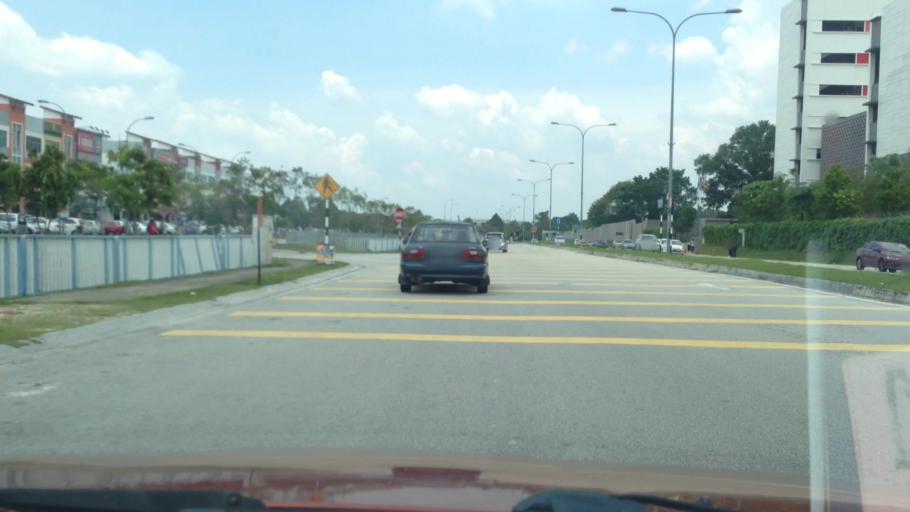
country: MY
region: Selangor
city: Kampung Baru Subang
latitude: 3.1771
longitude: 101.5487
